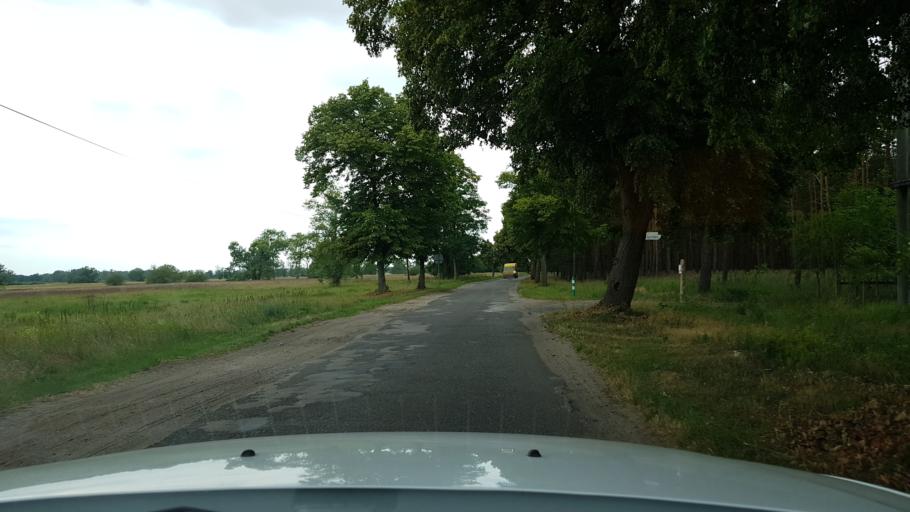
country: DE
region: Brandenburg
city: Manschnow
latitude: 52.6347
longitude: 14.5541
